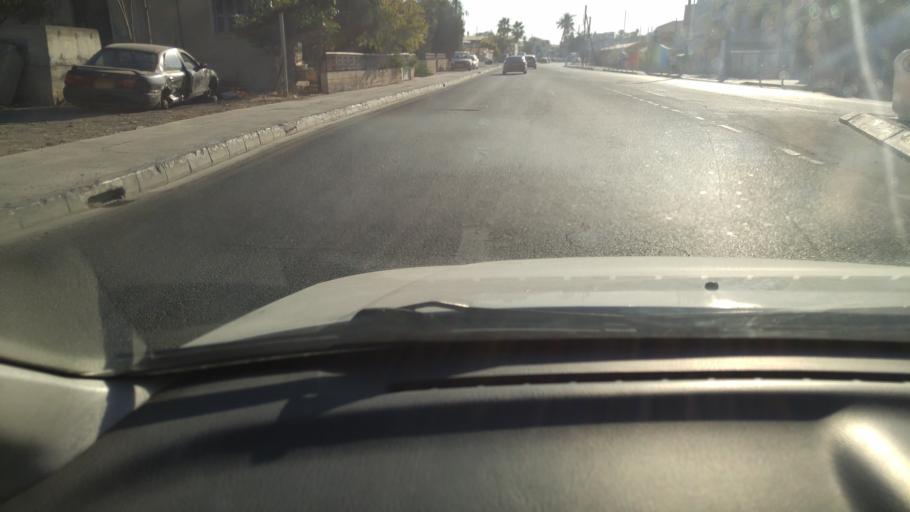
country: CY
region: Limassol
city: Limassol
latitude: 34.6718
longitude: 33.0348
